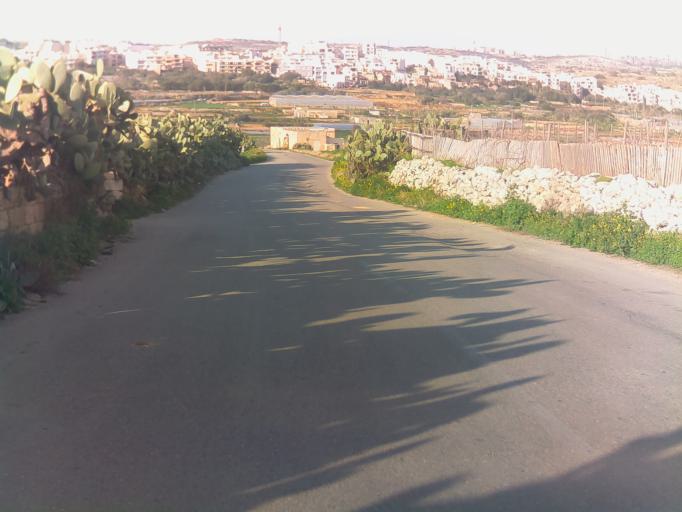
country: MT
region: L-Imgarr
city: Imgarr
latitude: 35.9322
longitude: 14.3509
